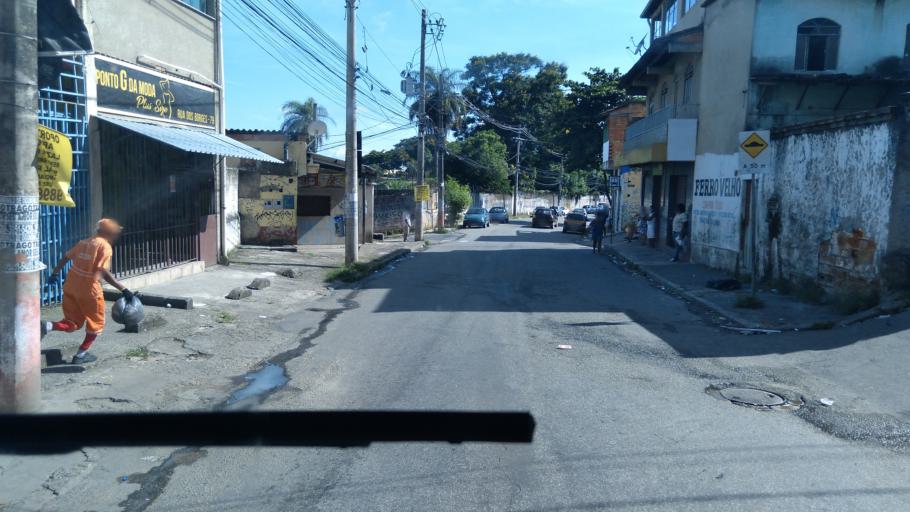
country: BR
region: Minas Gerais
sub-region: Belo Horizonte
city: Belo Horizonte
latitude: -19.8506
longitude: -43.8871
